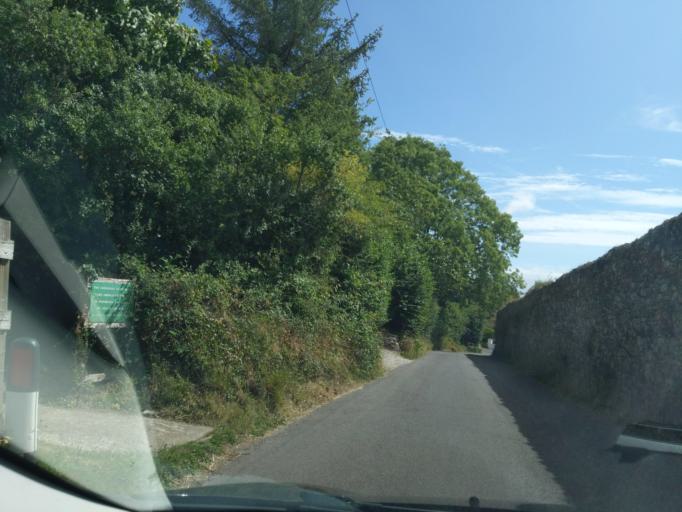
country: GB
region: England
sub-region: Devon
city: Modbury
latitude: 50.3554
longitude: -3.8879
